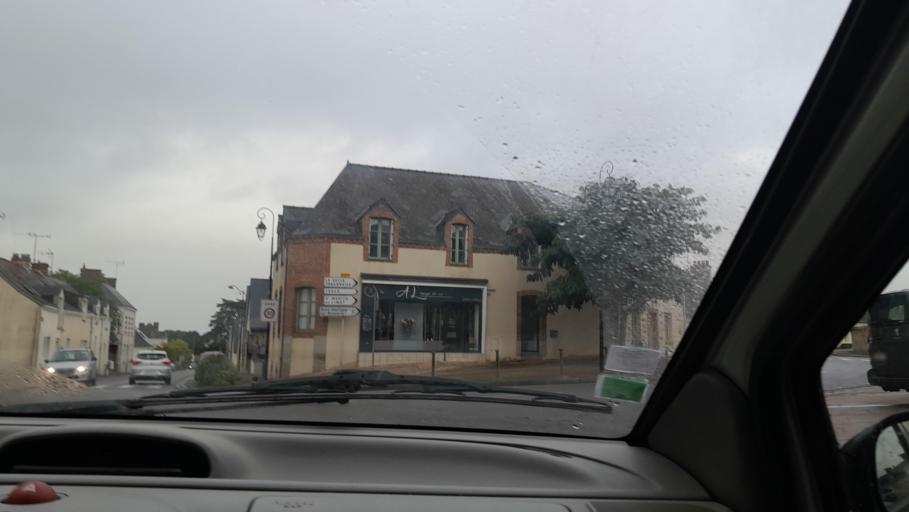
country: FR
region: Pays de la Loire
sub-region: Departement de la Mayenne
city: Congrier
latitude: 47.8421
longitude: -1.1372
